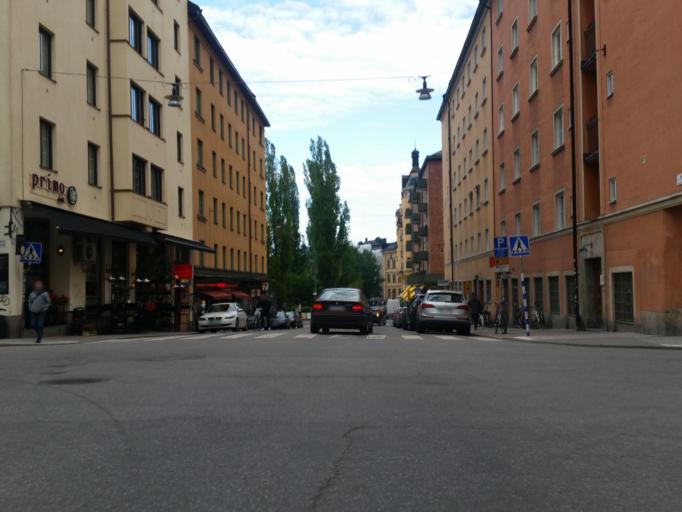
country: SE
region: Stockholm
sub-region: Stockholms Kommun
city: OEstermalm
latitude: 59.3134
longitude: 18.0822
